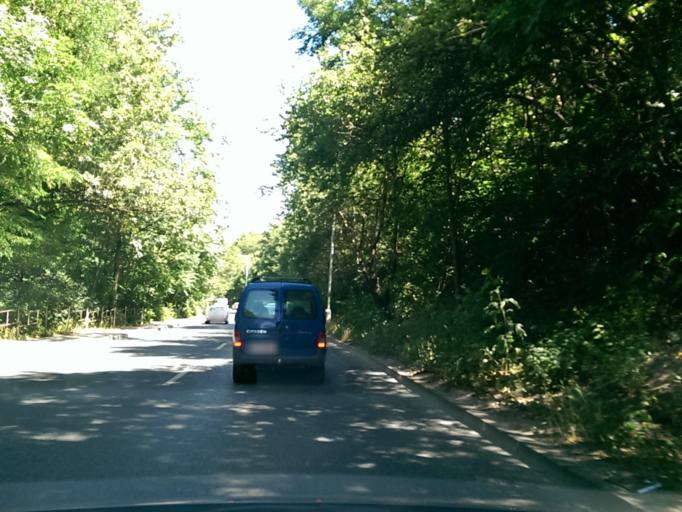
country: CZ
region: Praha
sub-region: Praha 8
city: Liben
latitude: 50.0928
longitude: 14.4716
